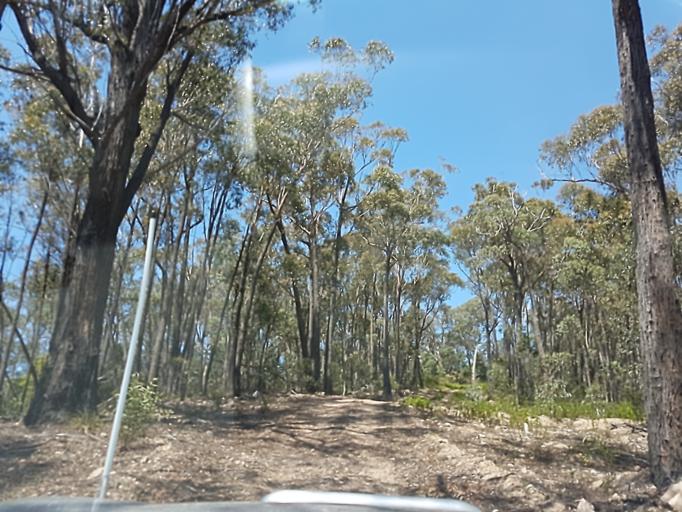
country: AU
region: Victoria
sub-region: East Gippsland
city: Lakes Entrance
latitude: -37.3086
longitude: 148.3599
